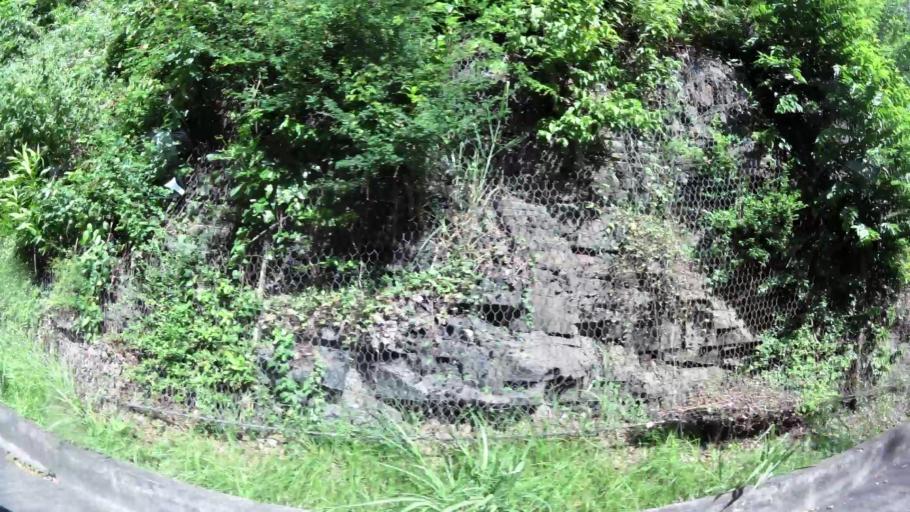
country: MQ
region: Martinique
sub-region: Martinique
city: Fort-de-France
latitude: 14.6228
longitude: -61.0723
